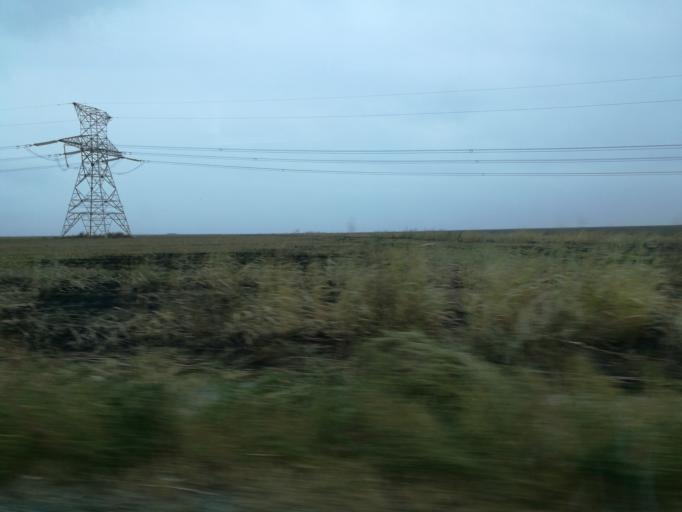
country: RO
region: Constanta
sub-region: Comuna Mihail Kogalniceanu
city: Piatra
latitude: 44.4563
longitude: 28.5555
